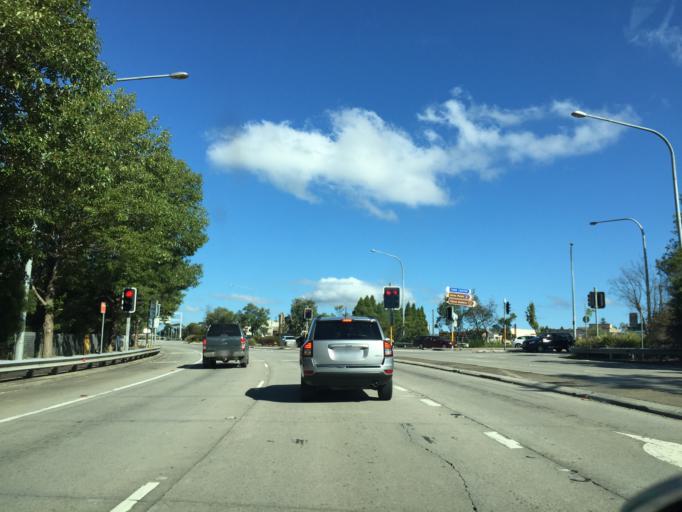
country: AU
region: New South Wales
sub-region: Blue Mountains Municipality
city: Katoomba
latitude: -33.7104
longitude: 150.3107
